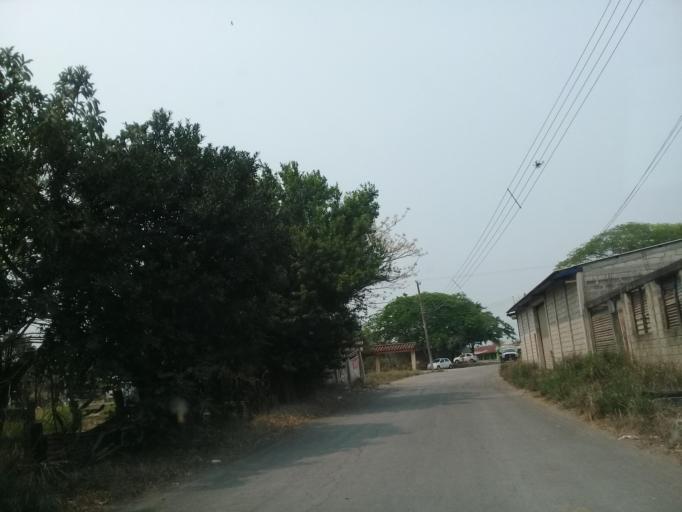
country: MX
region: Veracruz
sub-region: Medellin
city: La Laguna y Monte del Castillo
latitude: 18.9683
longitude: -96.1200
